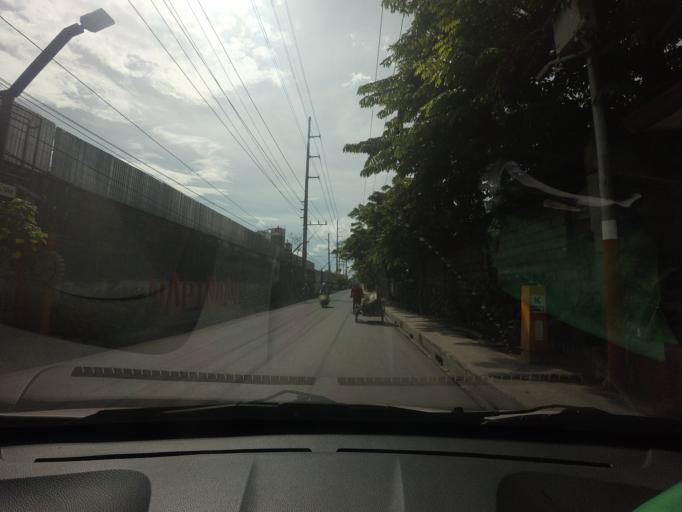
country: PH
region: Calabarzon
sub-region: Province of Rizal
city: Pateros
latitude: 14.5404
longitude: 121.0899
